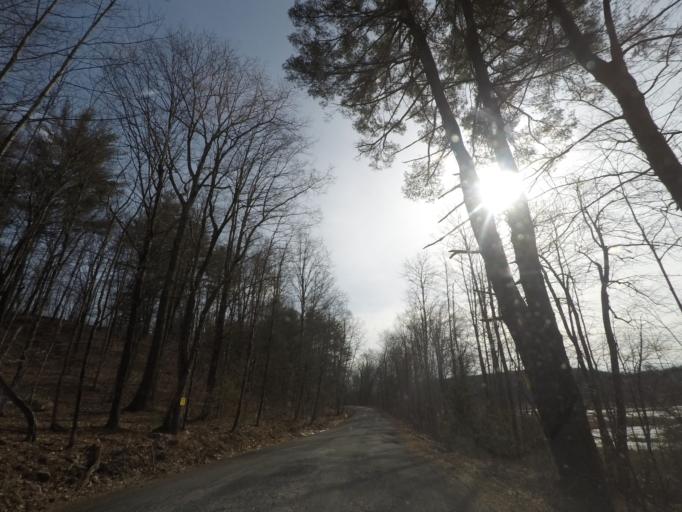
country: US
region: New York
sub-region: Rensselaer County
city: Nassau
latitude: 42.5174
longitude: -73.5636
